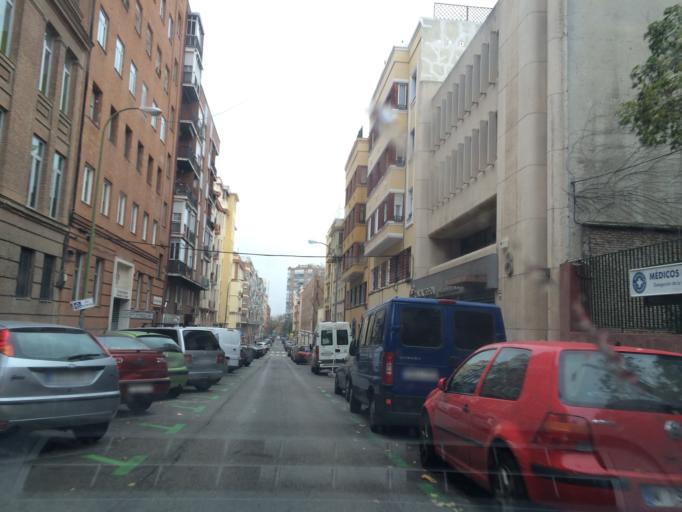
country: ES
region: Madrid
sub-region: Provincia de Madrid
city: Chamberi
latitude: 40.4479
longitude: -3.7094
